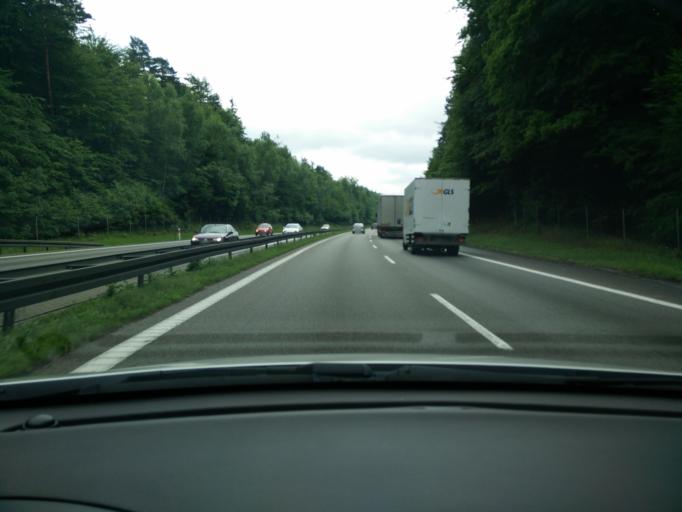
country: PL
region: Pomeranian Voivodeship
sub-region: Gdynia
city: Wielki Kack
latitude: 54.4501
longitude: 18.4928
